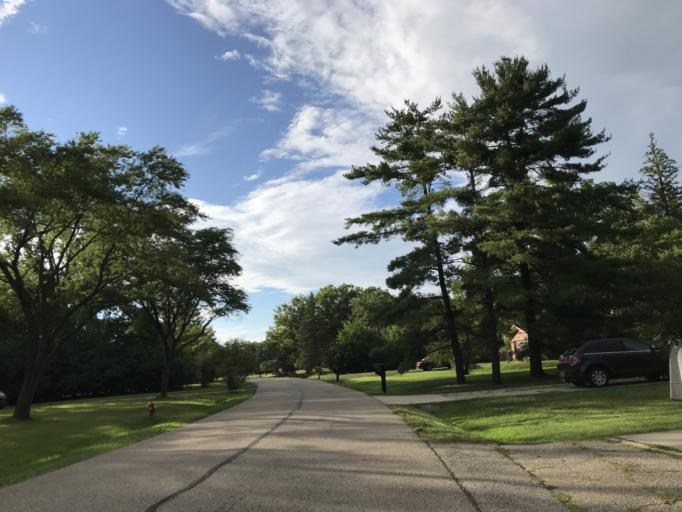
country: US
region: Michigan
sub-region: Oakland County
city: Farmington Hills
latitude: 42.4809
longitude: -83.3461
